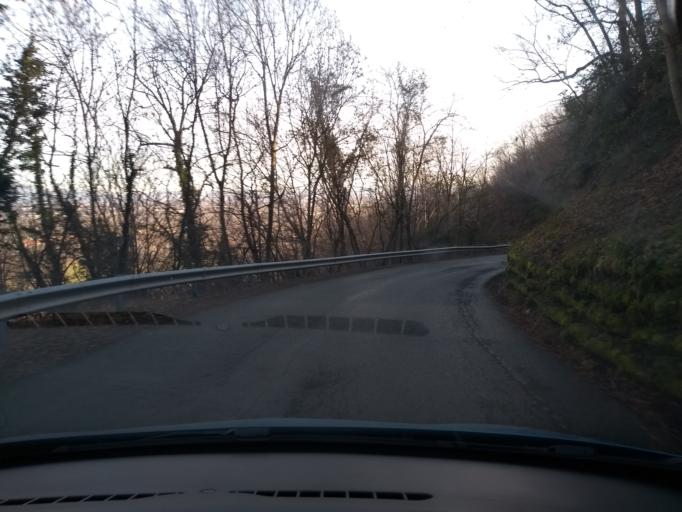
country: IT
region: Piedmont
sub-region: Provincia di Torino
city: Barbania
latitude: 45.2853
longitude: 7.6462
